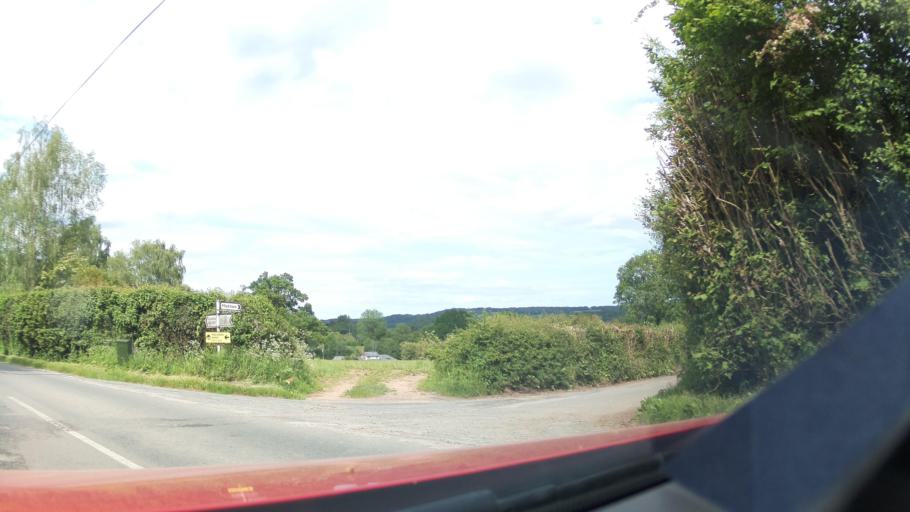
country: GB
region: England
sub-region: Herefordshire
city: Evesbatch
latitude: 52.1140
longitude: -2.4066
